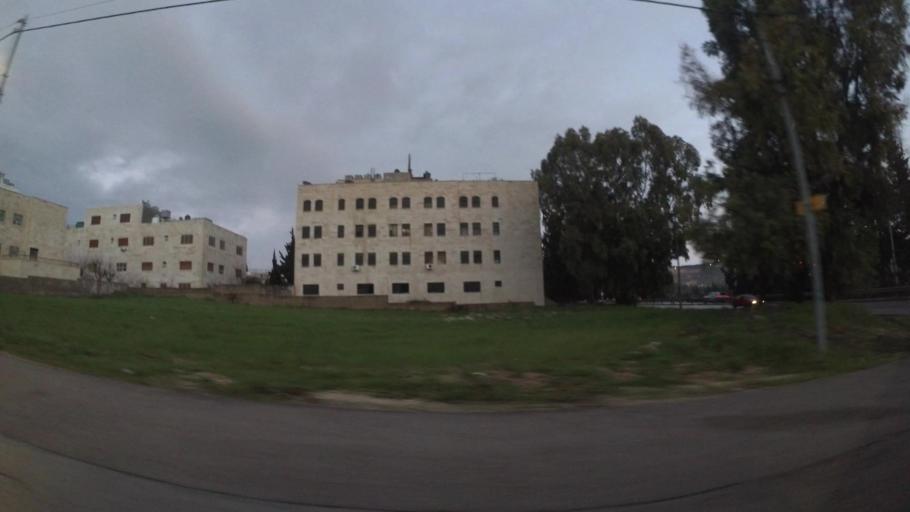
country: JO
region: Amman
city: Al Jubayhah
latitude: 32.0287
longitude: 35.8128
